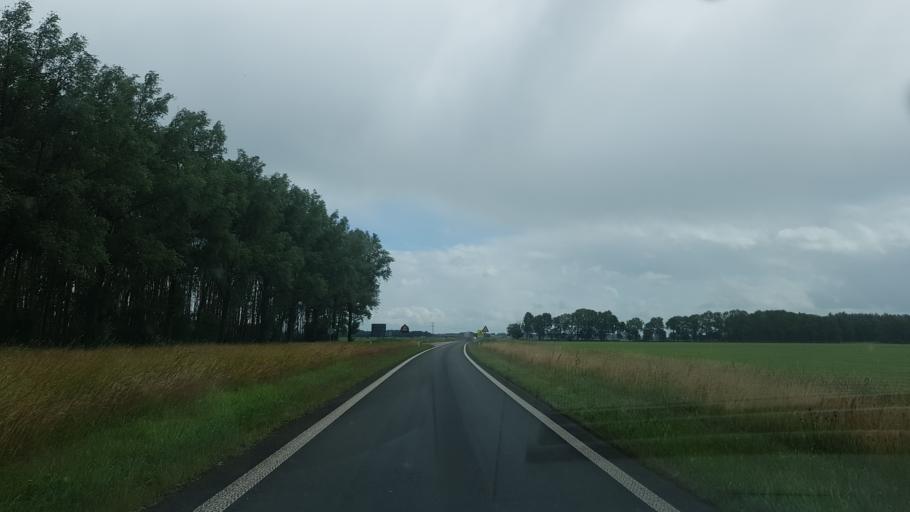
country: NL
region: Friesland
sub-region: Gemeente Dantumadiel
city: Rinsumageast
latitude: 53.3014
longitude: 5.9483
